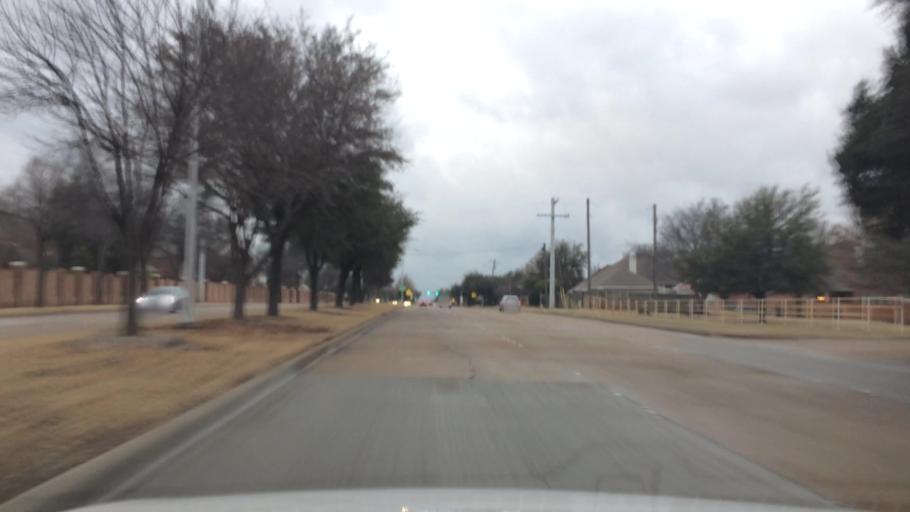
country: US
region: Texas
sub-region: Collin County
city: Frisco
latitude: 33.0964
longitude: -96.7716
